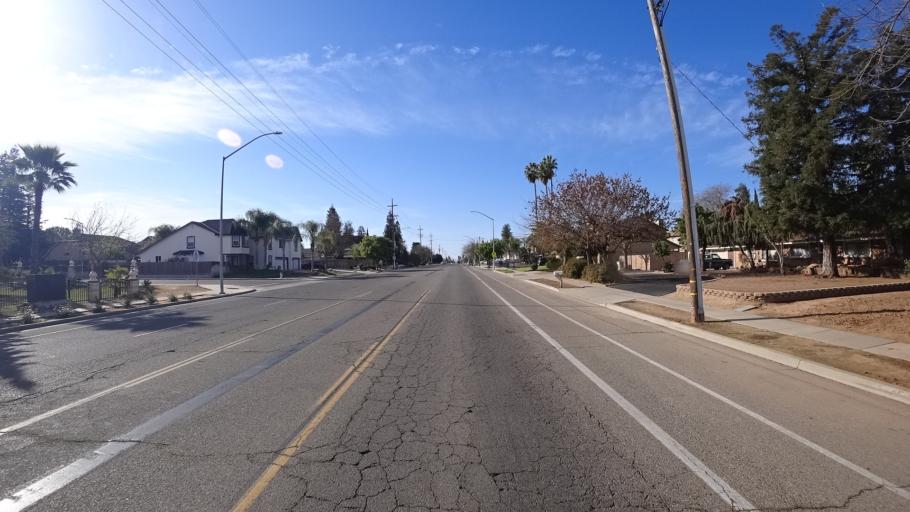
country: US
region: California
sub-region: Fresno County
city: West Park
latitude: 36.7921
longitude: -119.8804
